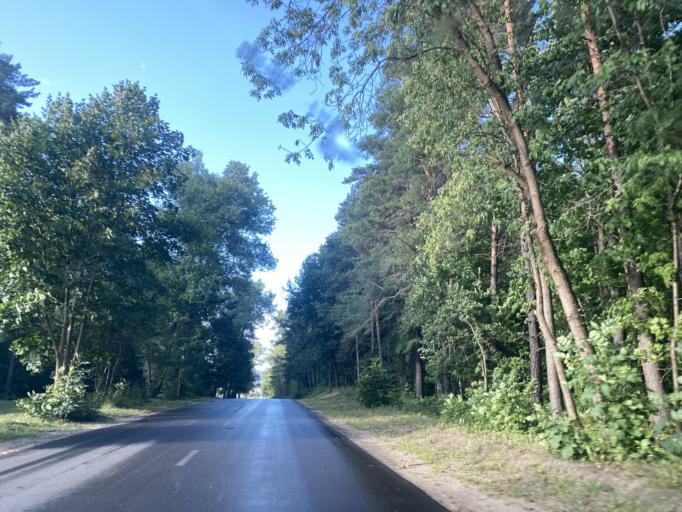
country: BY
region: Minsk
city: Borovlyany
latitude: 53.9241
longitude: 27.6541
